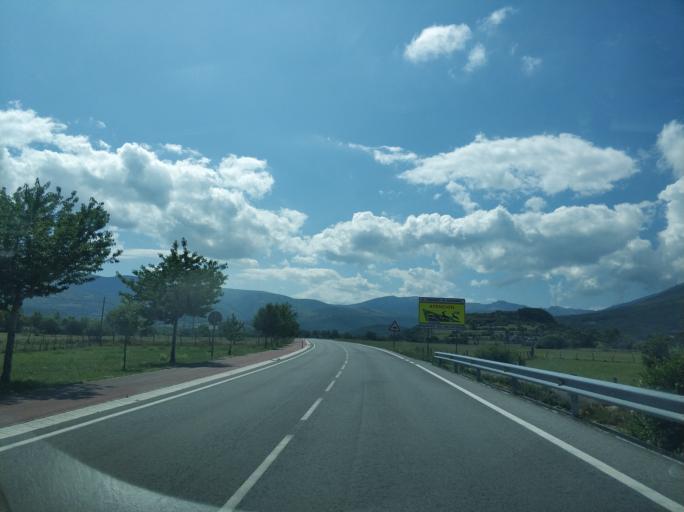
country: ES
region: Cantabria
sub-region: Provincia de Cantabria
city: Villaescusa
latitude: 43.0219
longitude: -4.2321
